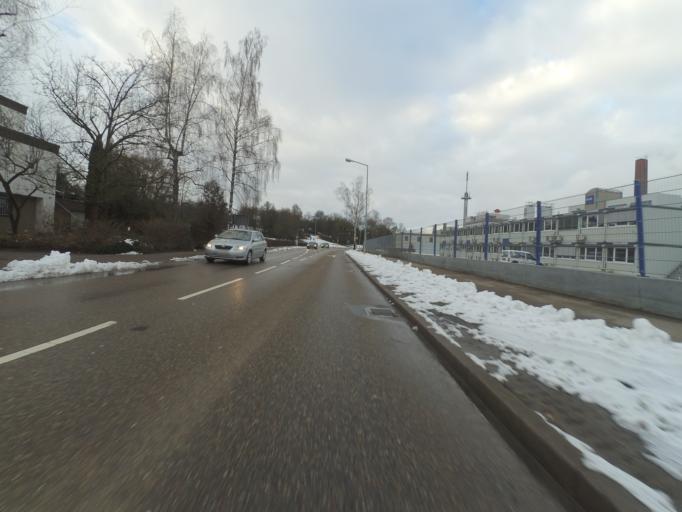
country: DE
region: Baden-Wuerttemberg
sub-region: Regierungsbezirk Stuttgart
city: Aalen
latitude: 48.8430
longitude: 10.0886
